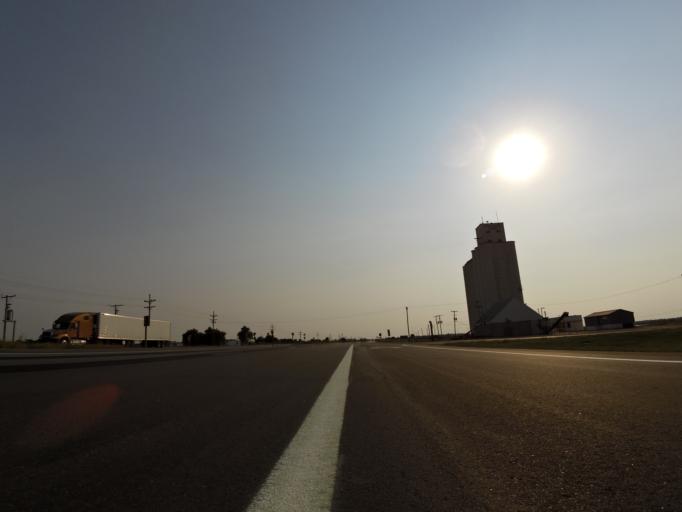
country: US
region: Kansas
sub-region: Reno County
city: South Hutchinson
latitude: 38.0076
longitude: -98.0130
